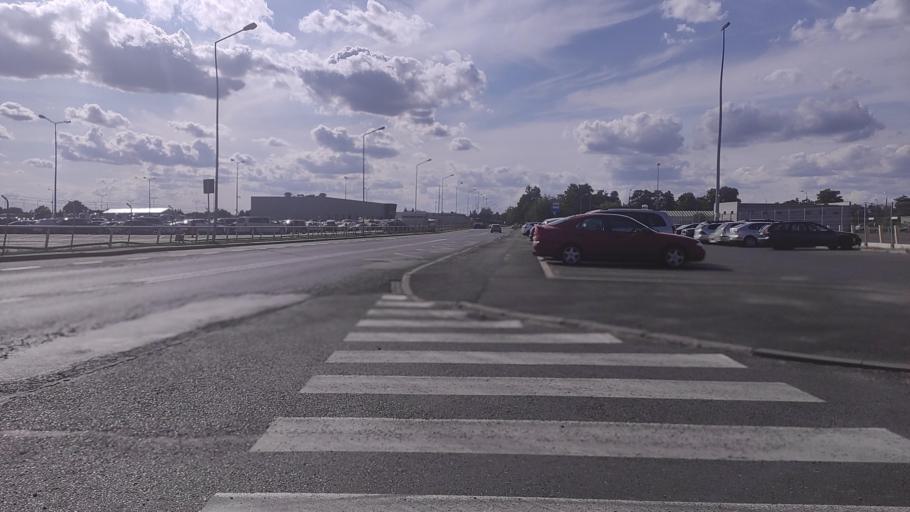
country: PL
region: Greater Poland Voivodeship
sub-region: Powiat poznanski
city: Swarzedz
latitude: 52.4005
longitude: 17.0928
